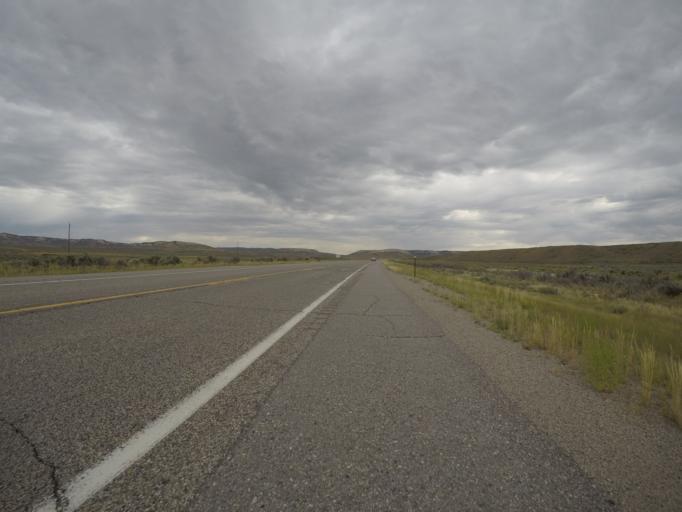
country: US
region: Wyoming
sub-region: Lincoln County
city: Kemmerer
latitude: 41.8158
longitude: -110.7166
